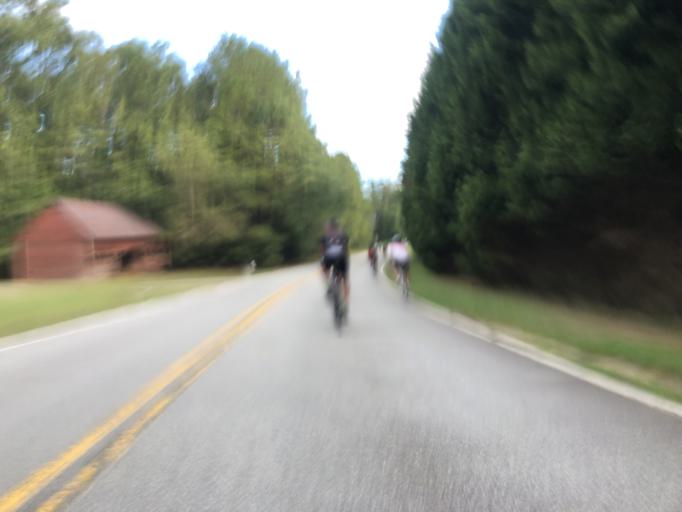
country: US
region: Georgia
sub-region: Fulton County
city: Fairburn
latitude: 33.6275
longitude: -84.6529
